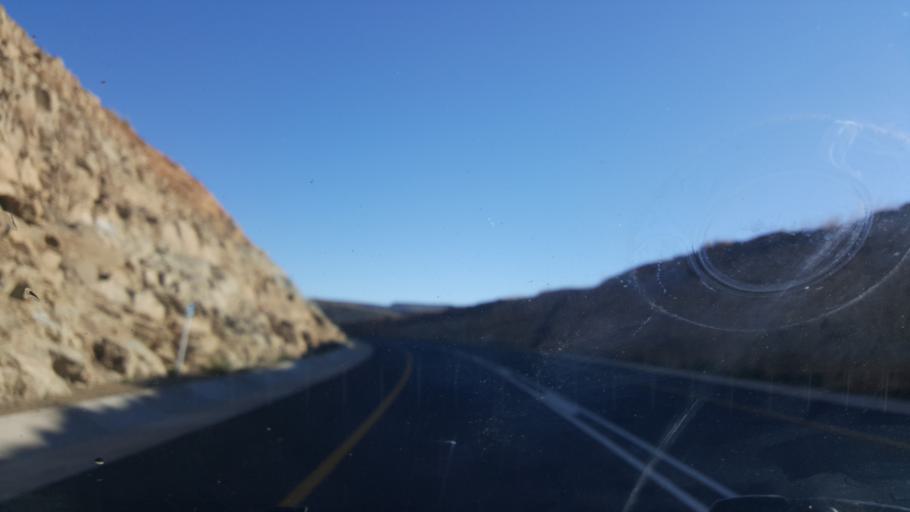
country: ZA
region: Eastern Cape
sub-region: Chris Hani District Municipality
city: Middelburg
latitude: -31.3793
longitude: 25.0344
